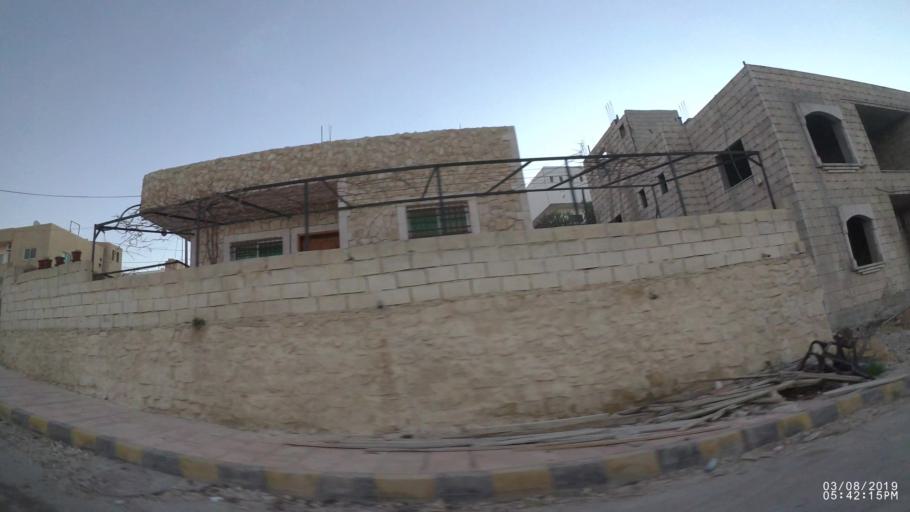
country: JO
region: Ma'an
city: Petra
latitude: 30.3182
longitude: 35.4749
